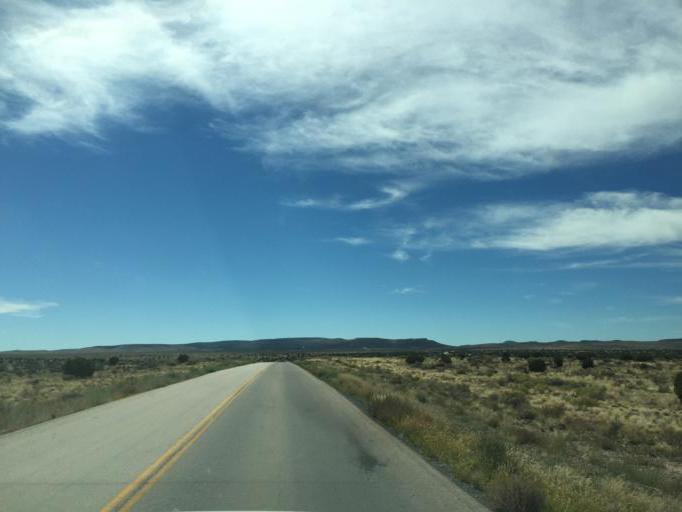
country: US
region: Arizona
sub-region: Mohave County
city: Meadview
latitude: 35.9656
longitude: -113.8225
